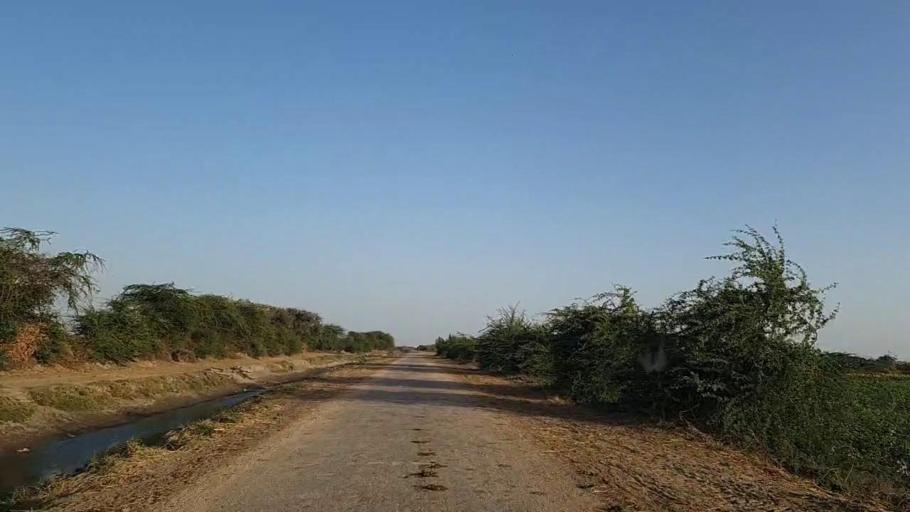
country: PK
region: Sindh
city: Jati
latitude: 24.4084
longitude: 68.3511
